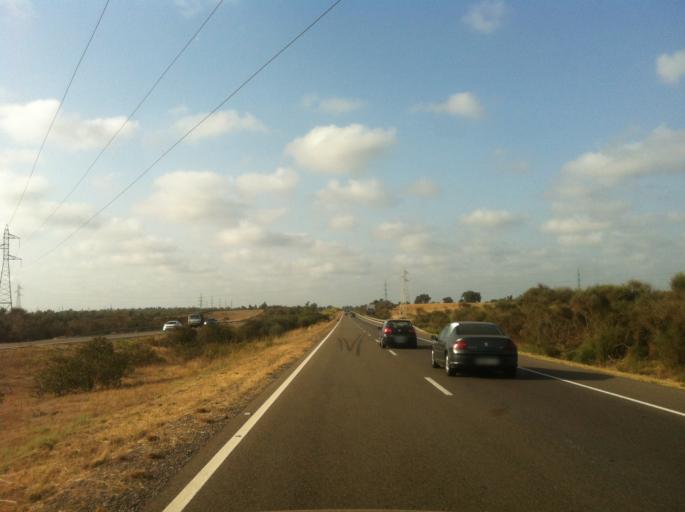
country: MA
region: Gharb-Chrarda-Beni Hssen
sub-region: Kenitra Province
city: Kenitra
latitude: 34.2277
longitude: -6.5562
